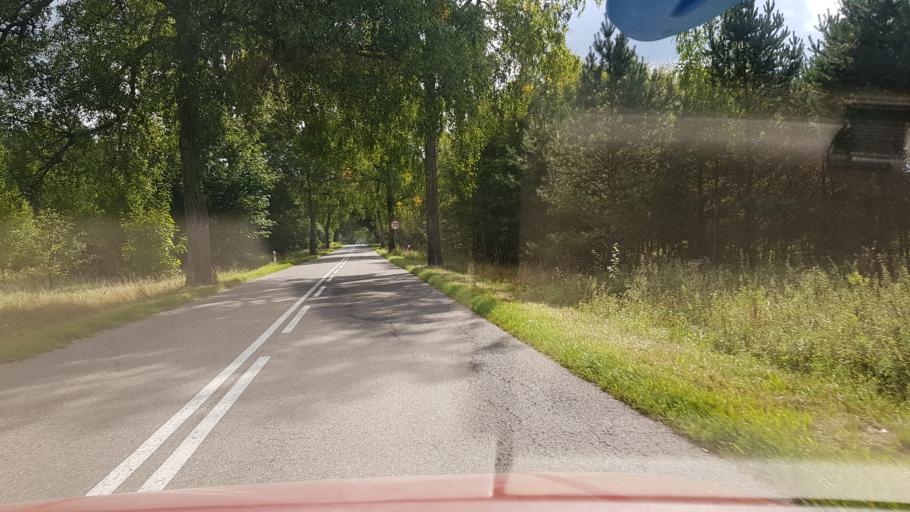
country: PL
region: West Pomeranian Voivodeship
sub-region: Powiat koszalinski
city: Polanow
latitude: 54.1168
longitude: 16.7569
